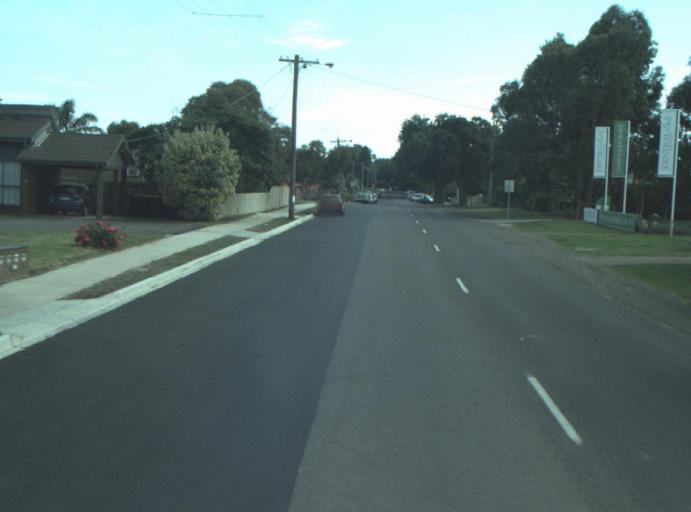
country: AU
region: Victoria
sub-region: Greater Geelong
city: Clifton Springs
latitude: -38.1765
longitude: 144.5701
